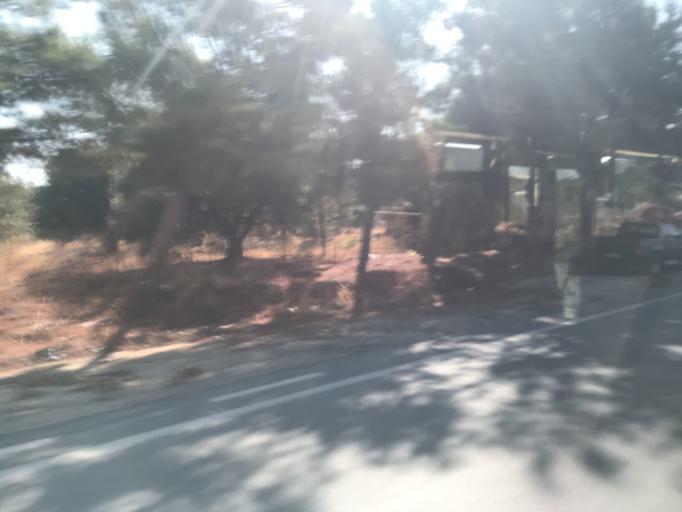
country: GR
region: Crete
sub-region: Nomos Irakleiou
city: Gazi
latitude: 35.3117
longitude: 25.0913
